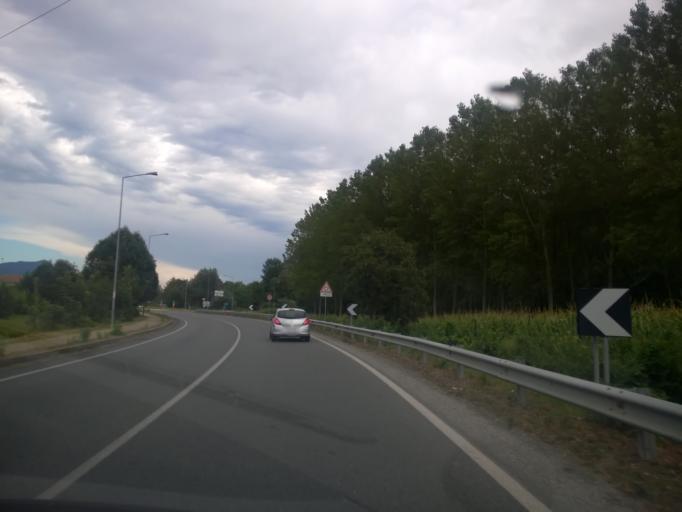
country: IT
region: Piedmont
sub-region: Provincia di Torino
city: Condove
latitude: 45.1096
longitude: 7.3139
